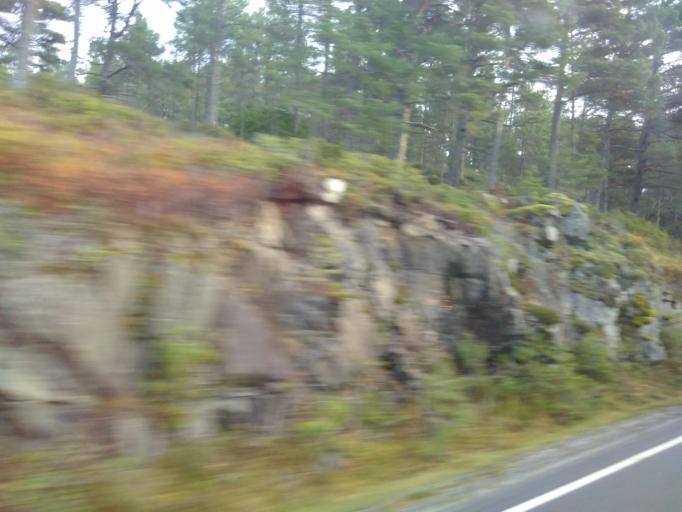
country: NO
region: Sor-Trondelag
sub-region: Hitra
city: Fillan
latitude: 63.5722
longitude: 9.0239
